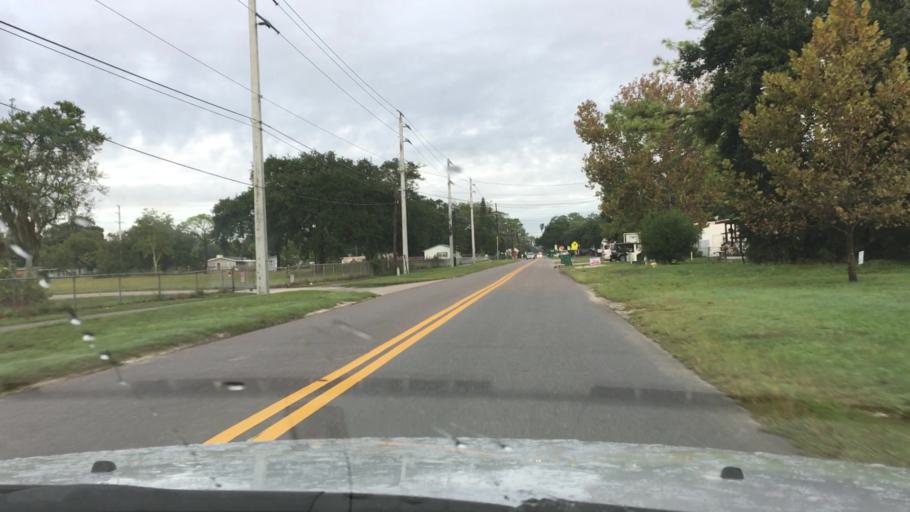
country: US
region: Florida
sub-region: Volusia County
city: Holly Hill
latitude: 29.2439
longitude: -81.0510
